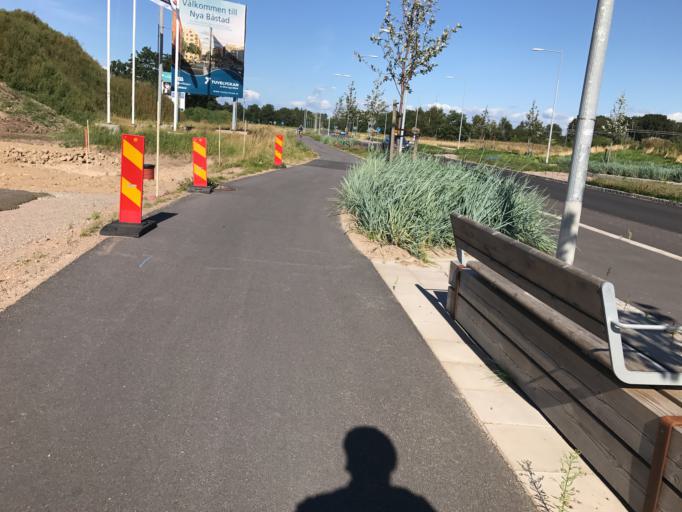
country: SE
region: Skane
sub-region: Bastads Kommun
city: Bastad
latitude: 56.4328
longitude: 12.9064
